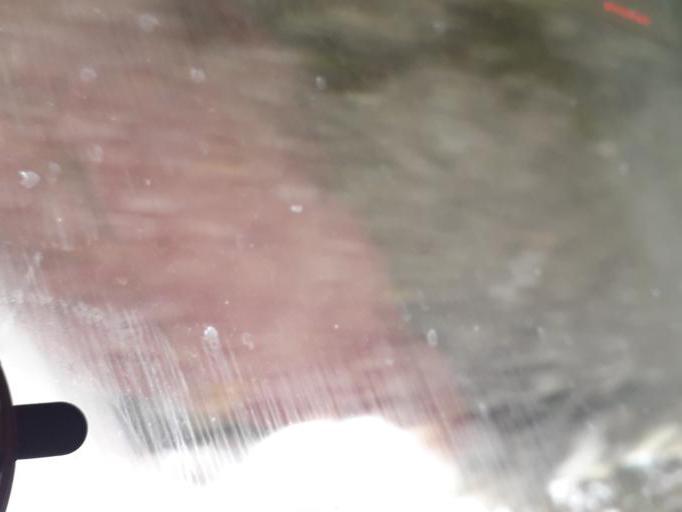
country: IE
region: Leinster
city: Ballyboden
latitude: 53.2637
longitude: -6.2882
